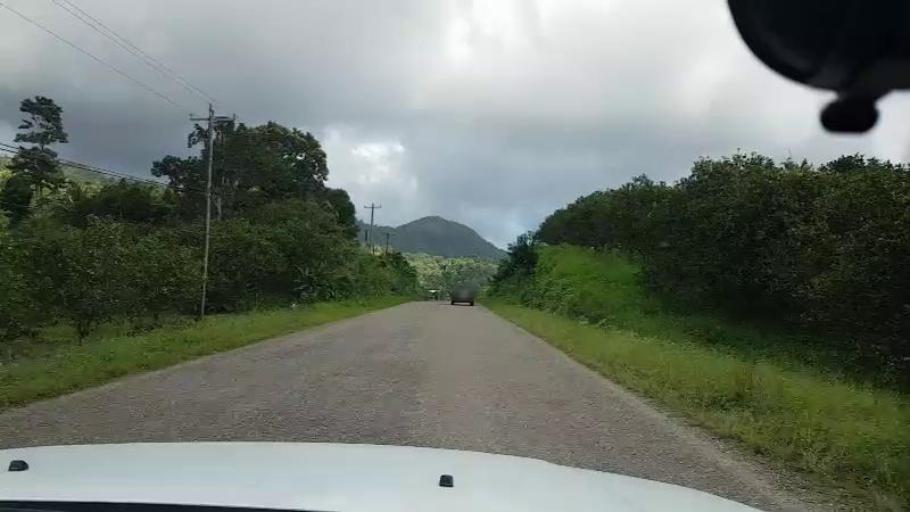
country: BZ
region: Stann Creek
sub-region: Dangriga
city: Dangriga
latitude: 16.9978
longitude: -88.4127
